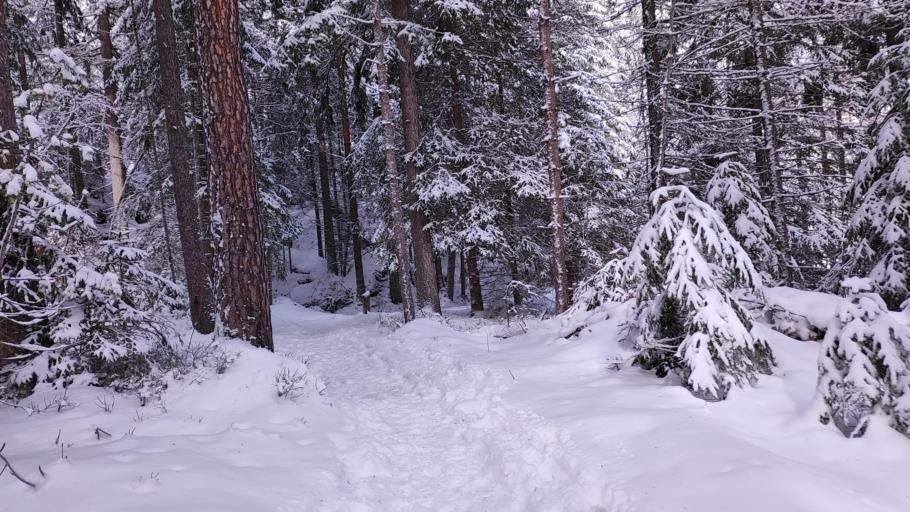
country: AT
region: Tyrol
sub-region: Politischer Bezirk Imst
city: Umhausen
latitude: 47.1025
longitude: 10.9333
